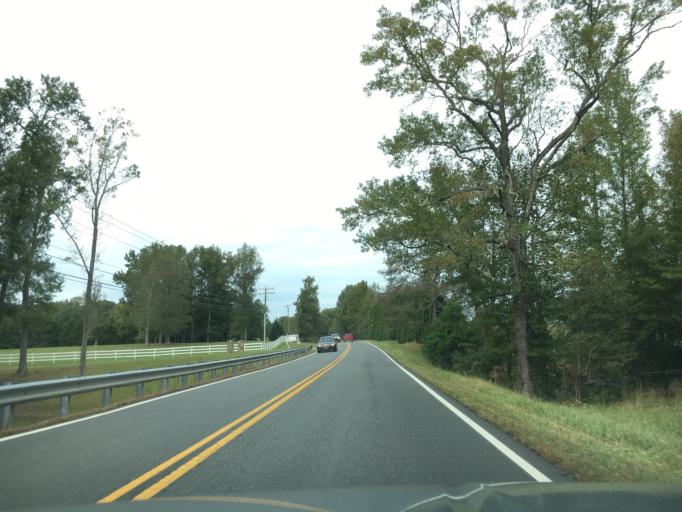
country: US
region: Virginia
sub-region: Goochland County
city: Goochland
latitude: 37.7403
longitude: -77.8450
